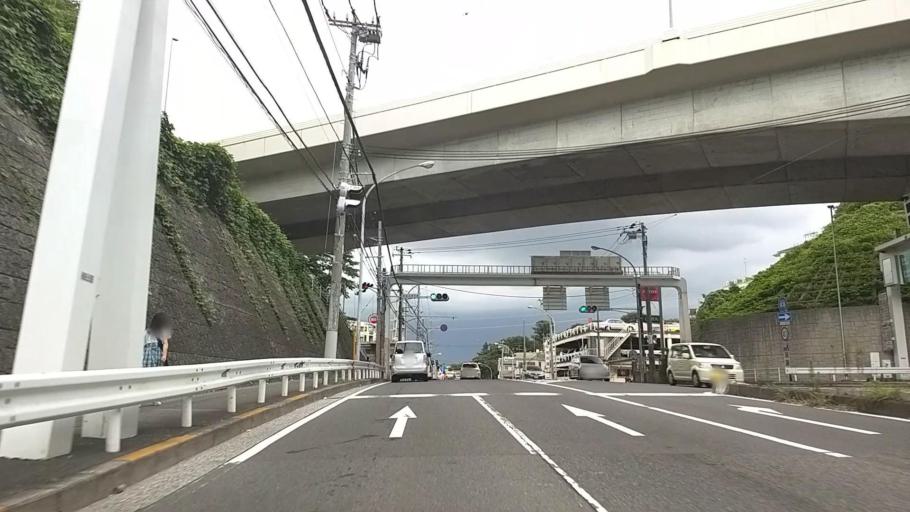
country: JP
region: Kanagawa
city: Yokohama
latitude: 35.4398
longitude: 139.5960
